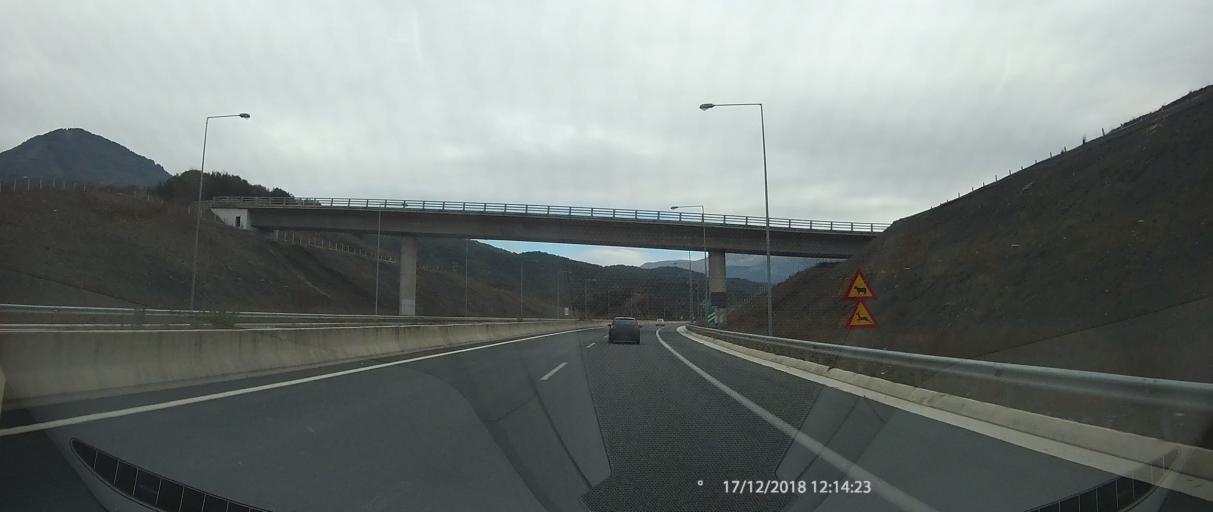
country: GR
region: Epirus
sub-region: Nomos Ioanninon
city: Katsikas
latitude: 39.7180
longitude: 20.9960
